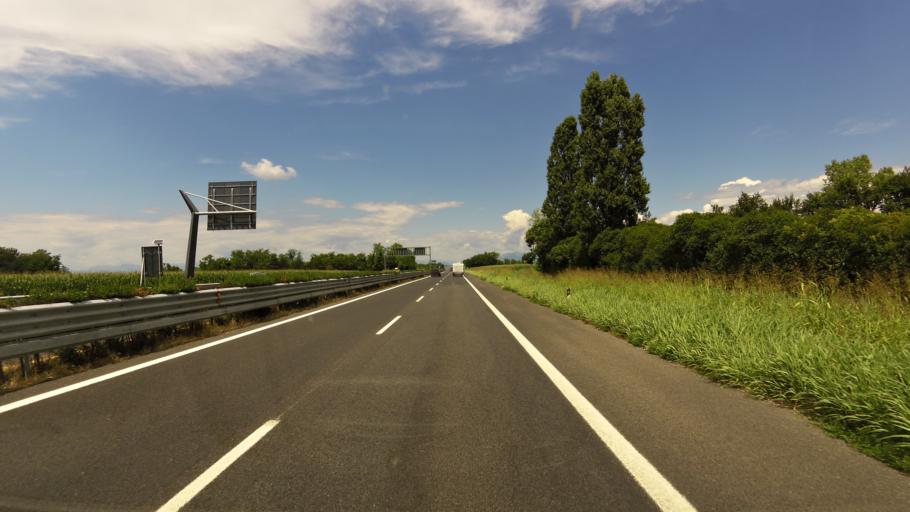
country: IT
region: Friuli Venezia Giulia
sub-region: Provincia di Udine
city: Santa Maria la Longa
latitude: 45.9098
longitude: 13.2818
